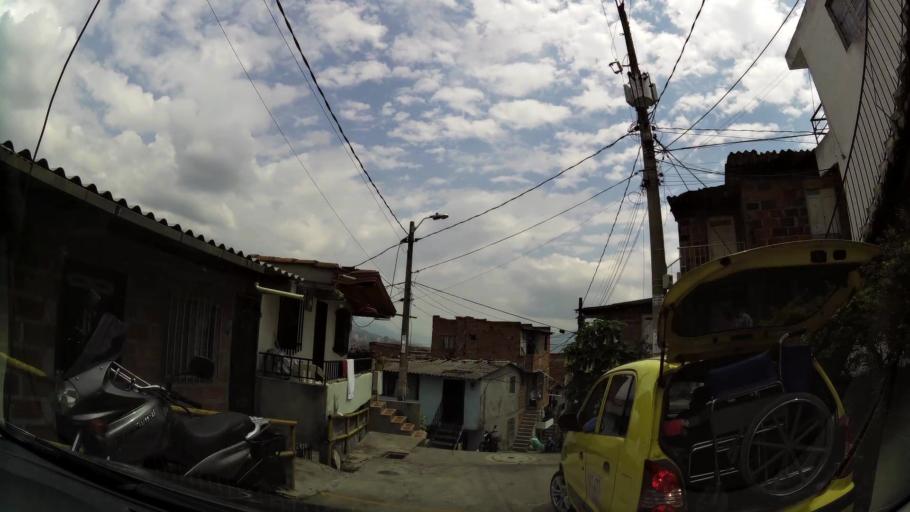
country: CO
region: Antioquia
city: Medellin
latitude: 6.2492
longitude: -75.6202
